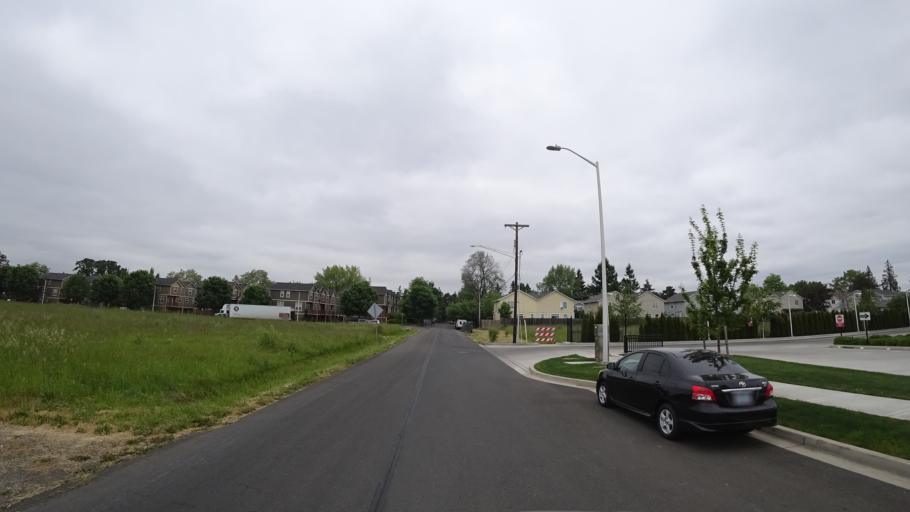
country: US
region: Oregon
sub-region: Washington County
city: Aloha
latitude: 45.4988
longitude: -122.9098
